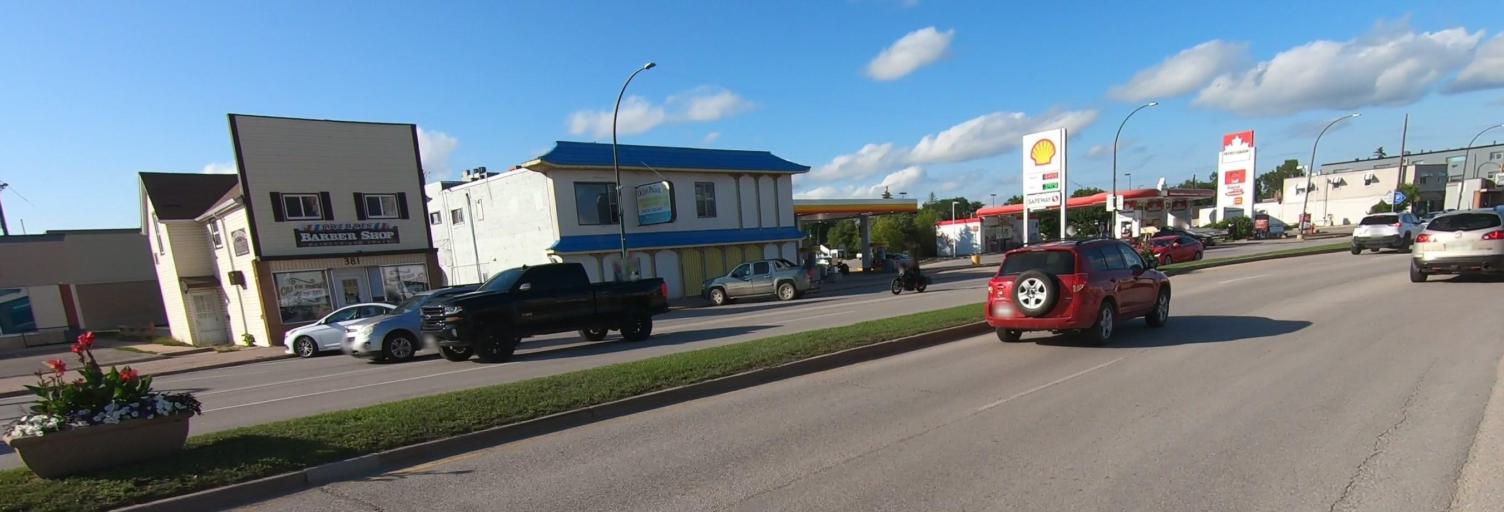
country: CA
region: Manitoba
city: Selkirk
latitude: 50.1440
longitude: -96.8740
